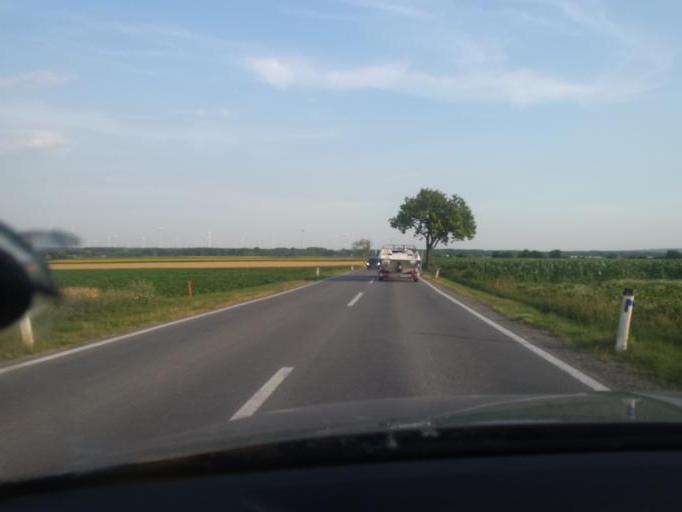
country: AT
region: Lower Austria
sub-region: Politischer Bezirk Bruck an der Leitha
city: Rohrau
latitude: 48.0915
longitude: 16.8620
